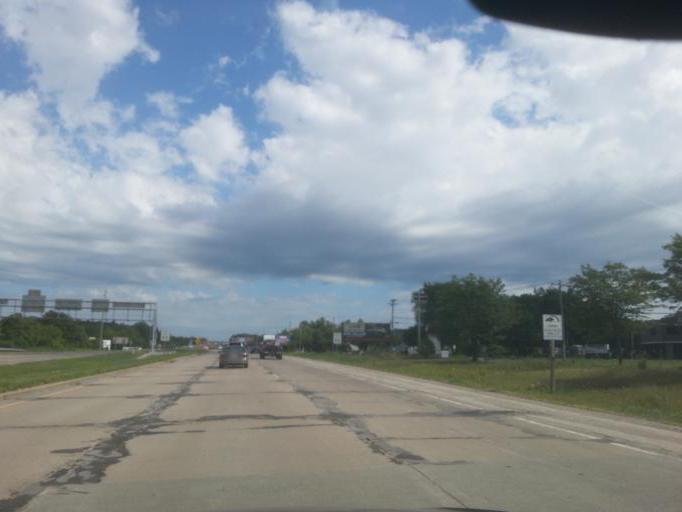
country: US
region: Wisconsin
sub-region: Dane County
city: Monona
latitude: 43.0490
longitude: -89.3078
